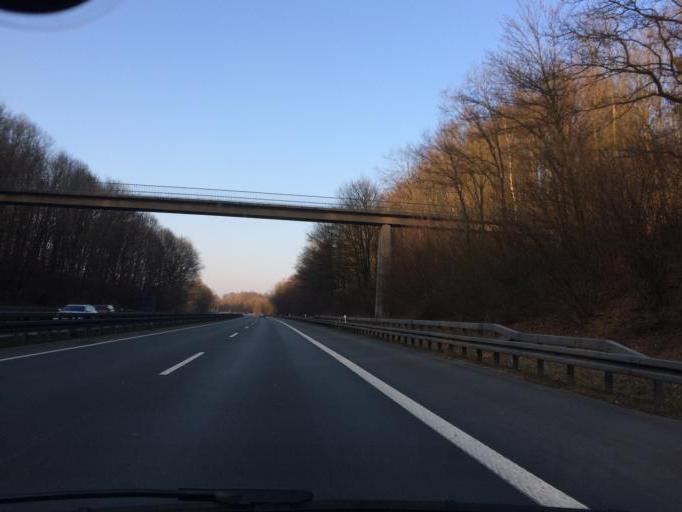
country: DE
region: North Rhine-Westphalia
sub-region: Regierungsbezirk Munster
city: Haltern
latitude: 51.7509
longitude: 7.1655
